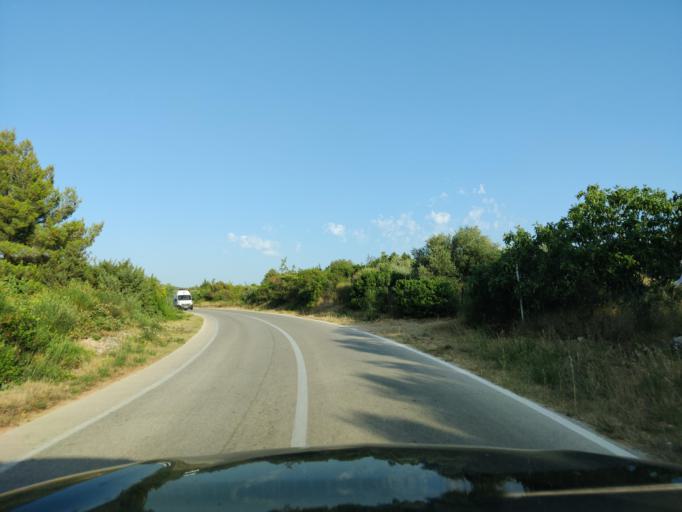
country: HR
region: Sibensko-Kniniska
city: Tribunj
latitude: 43.7846
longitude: 15.7084
